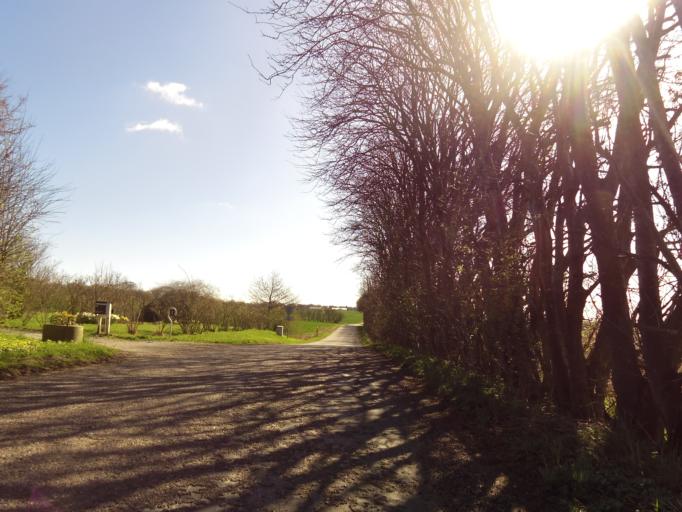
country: DK
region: Central Jutland
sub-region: Holstebro Kommune
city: Vinderup
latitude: 56.4356
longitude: 8.7614
